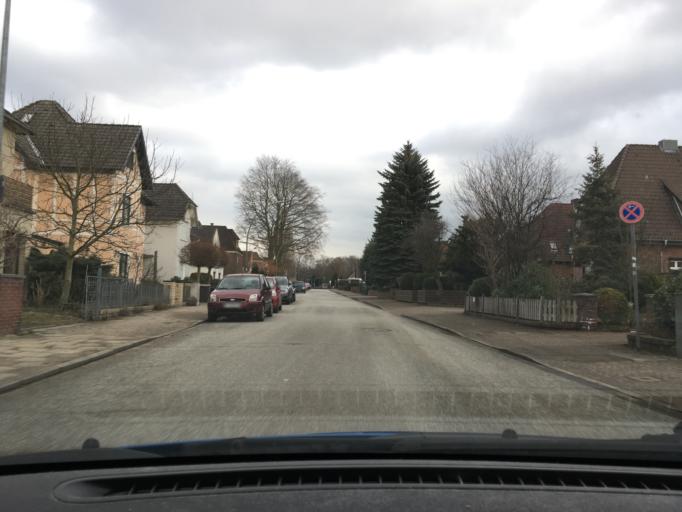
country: DE
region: Schleswig-Holstein
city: Wedel
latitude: 53.5746
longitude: 9.7084
